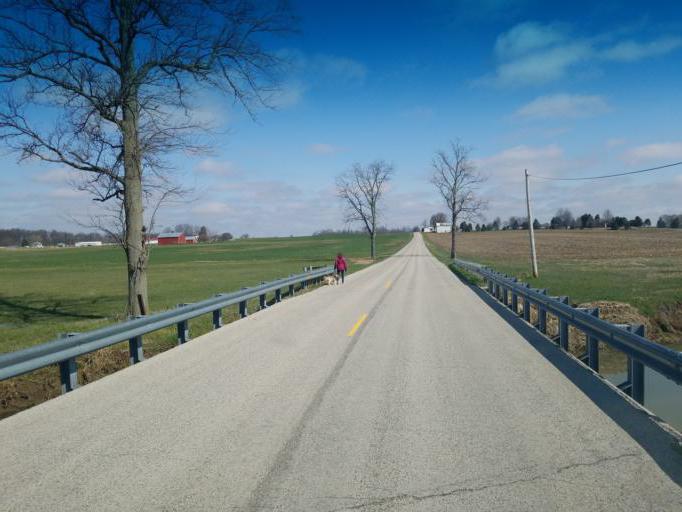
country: US
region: Ohio
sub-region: Crawford County
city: Bucyrus
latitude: 40.8943
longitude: -82.9401
